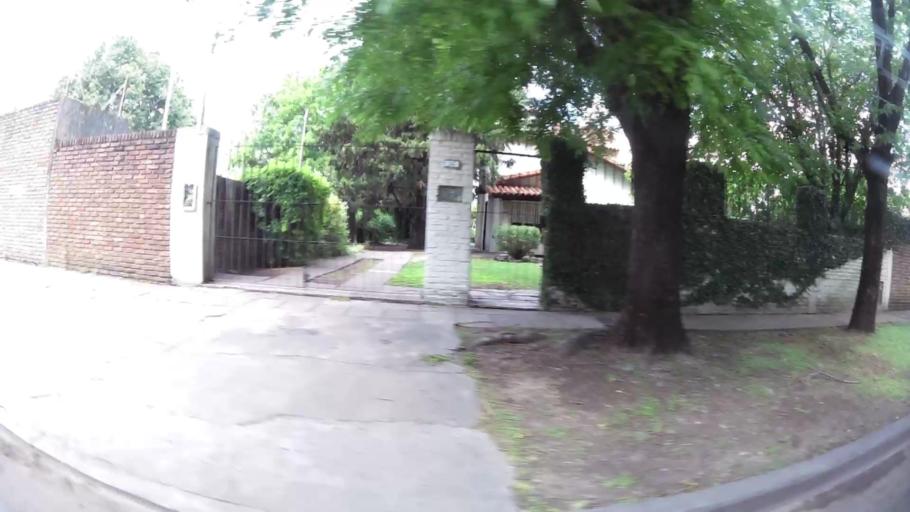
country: AR
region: Buenos Aires
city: Ituzaingo
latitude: -34.6401
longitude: -58.6712
